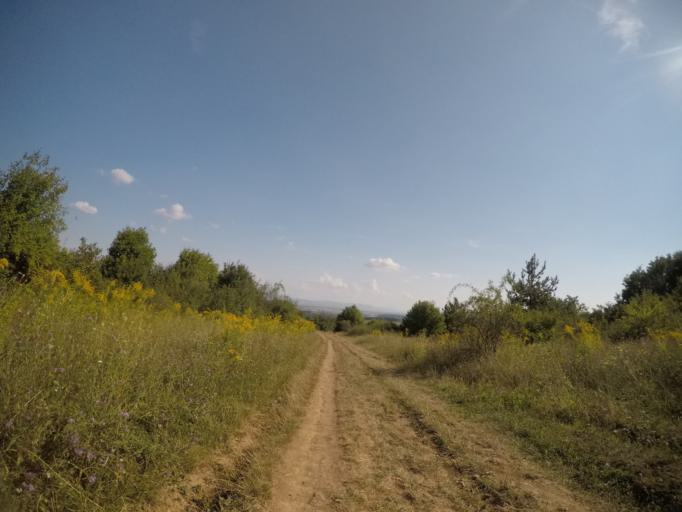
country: SK
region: Kosicky
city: Kosice
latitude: 48.7406
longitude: 21.2087
